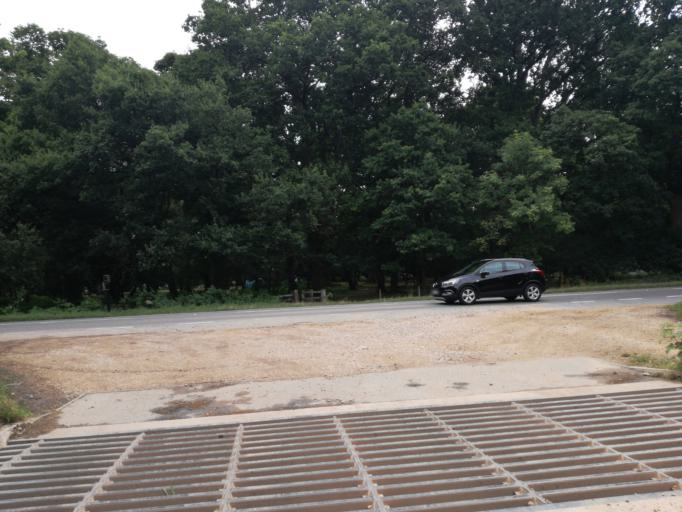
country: GB
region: England
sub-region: Hampshire
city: Brockenhurst
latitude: 50.8374
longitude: -1.5730
